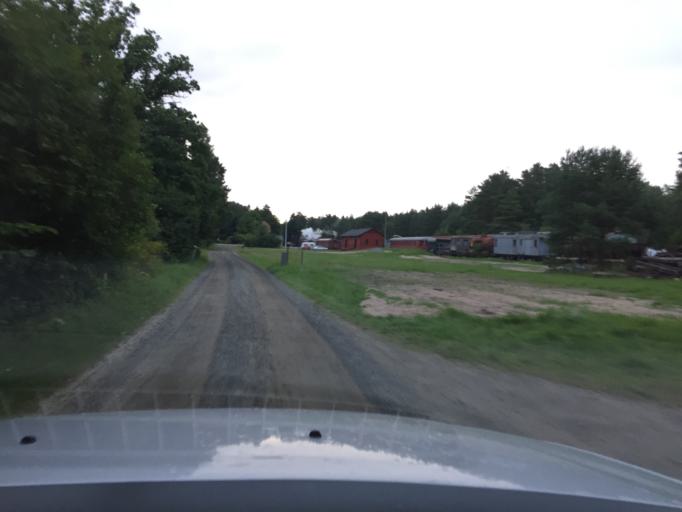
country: SE
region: Skane
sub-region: Kristianstads Kommun
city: Degeberga
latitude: 55.7328
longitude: 14.1246
